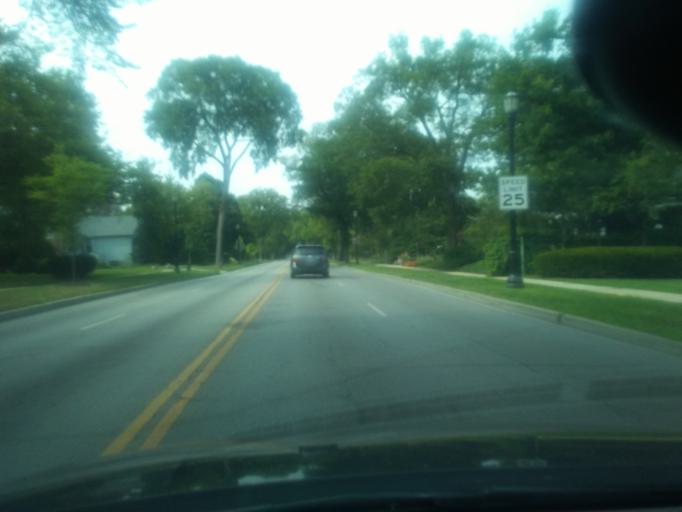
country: US
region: Illinois
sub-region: Cook County
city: Evanston
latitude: 42.0343
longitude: -87.6868
